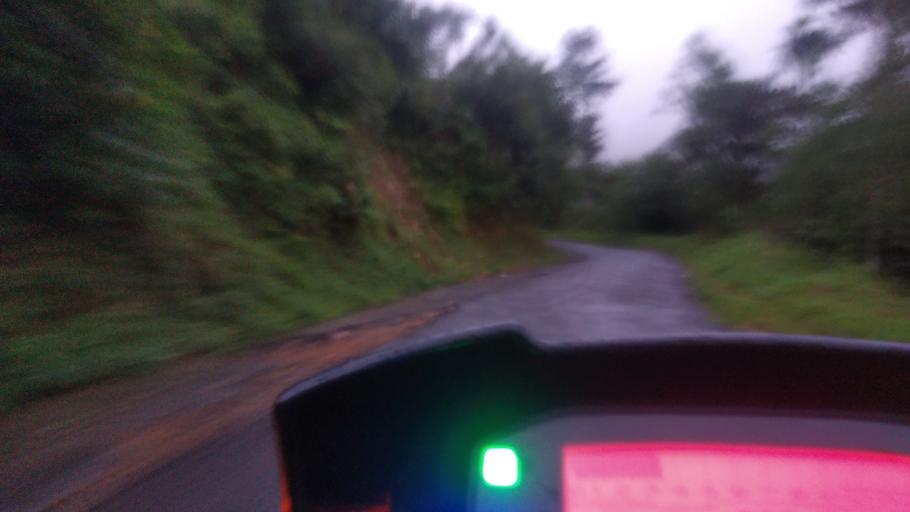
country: IN
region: Kerala
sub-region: Kottayam
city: Erattupetta
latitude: 9.5415
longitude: 76.9681
